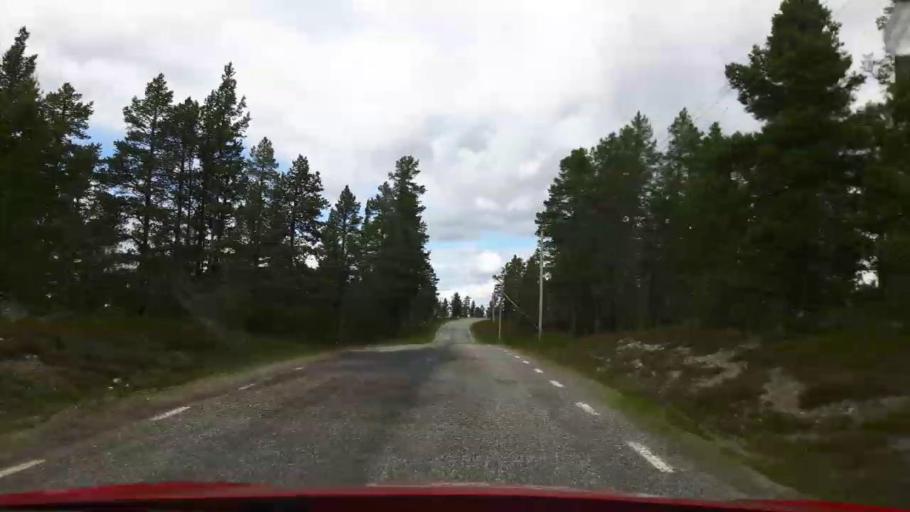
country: NO
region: Hedmark
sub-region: Engerdal
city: Engerdal
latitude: 62.3141
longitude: 12.8095
